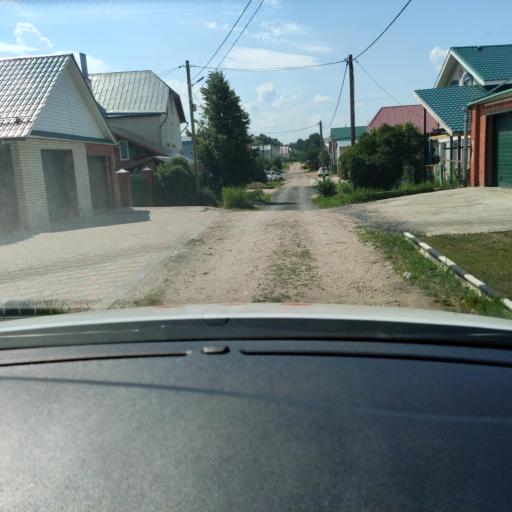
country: RU
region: Tatarstan
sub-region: Gorod Kazan'
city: Kazan
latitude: 55.8837
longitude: 49.0619
